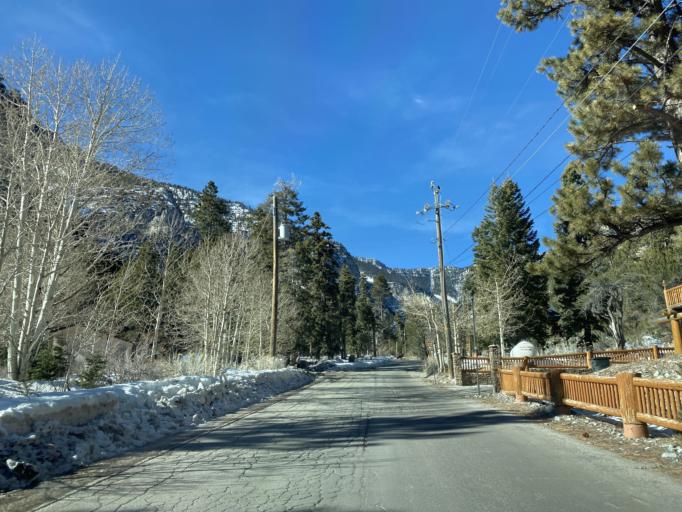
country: US
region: Nevada
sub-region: Nye County
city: Pahrump
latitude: 36.2626
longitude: -115.6537
